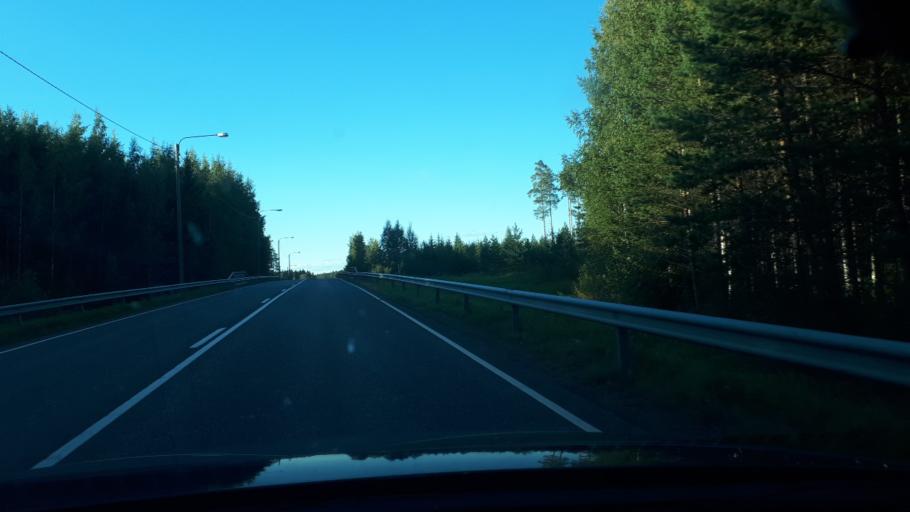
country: FI
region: Northern Savo
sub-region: Ylae-Savo
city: Lapinlahti
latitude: 63.4303
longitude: 27.3280
